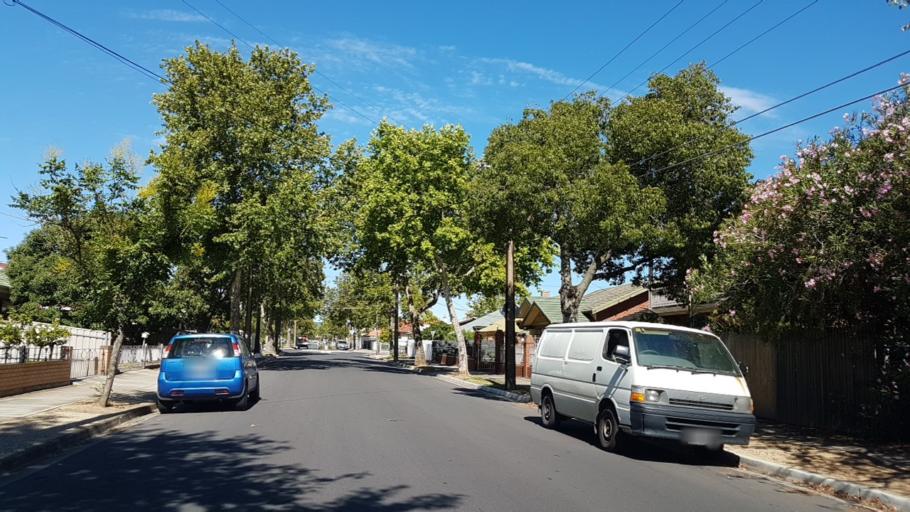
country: AU
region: South Australia
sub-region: City of West Torrens
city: Thebarton
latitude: -34.9203
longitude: 138.5610
